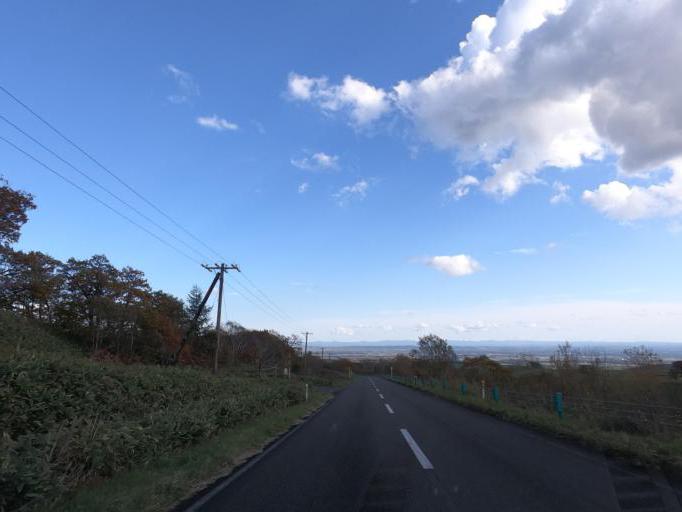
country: JP
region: Hokkaido
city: Otofuke
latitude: 43.2924
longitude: 143.1987
